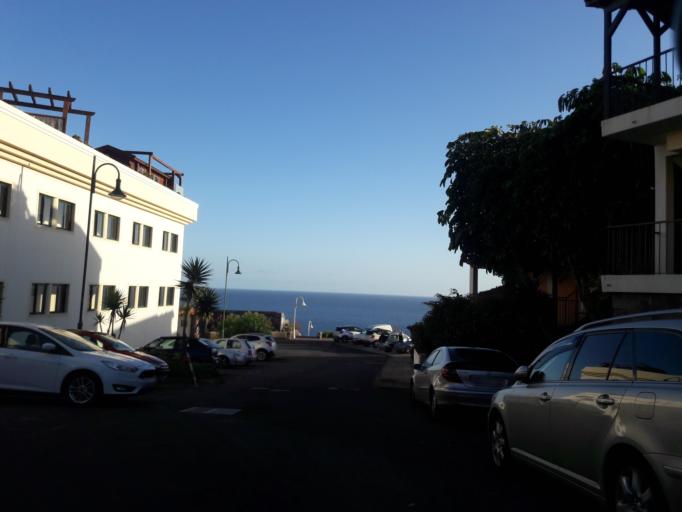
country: PT
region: Madeira
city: Canico
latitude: 32.6419
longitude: -16.8320
